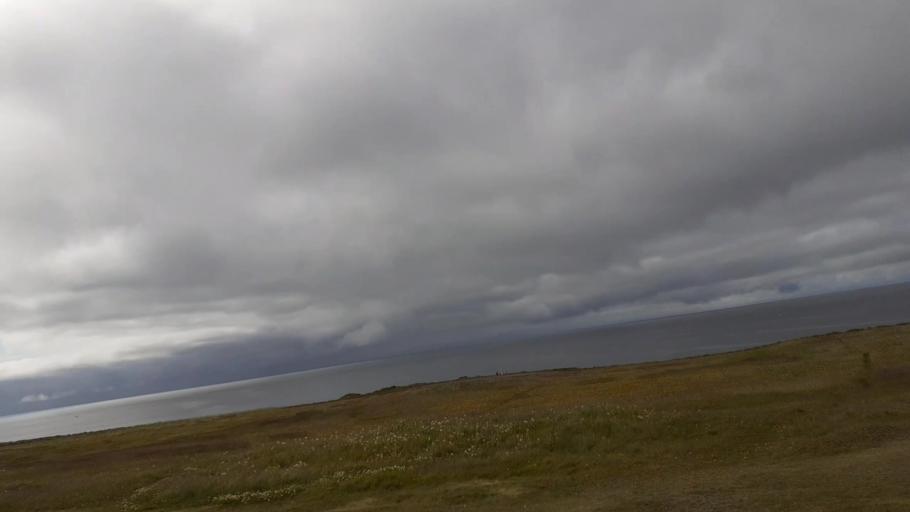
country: IS
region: Northeast
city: Dalvik
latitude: 66.5486
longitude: -18.0214
